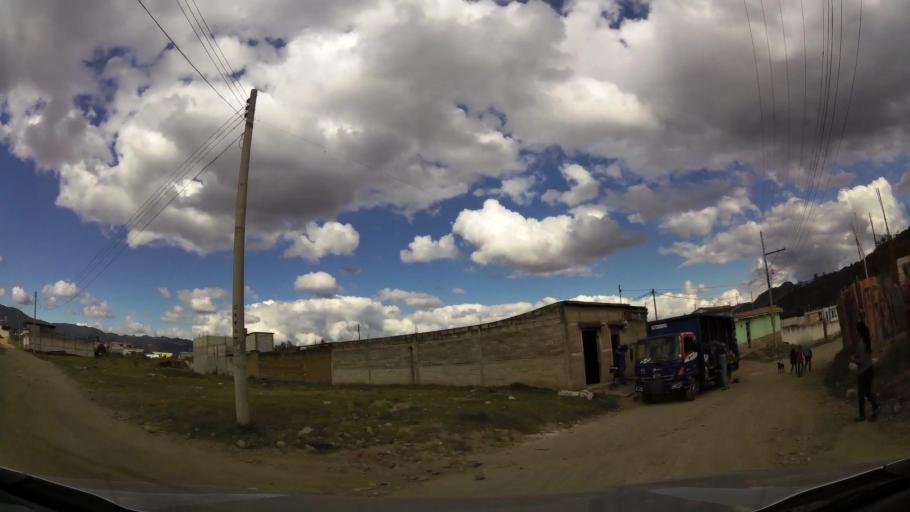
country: GT
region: Quetzaltenango
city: Quetzaltenango
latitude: 14.8281
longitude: -91.5391
